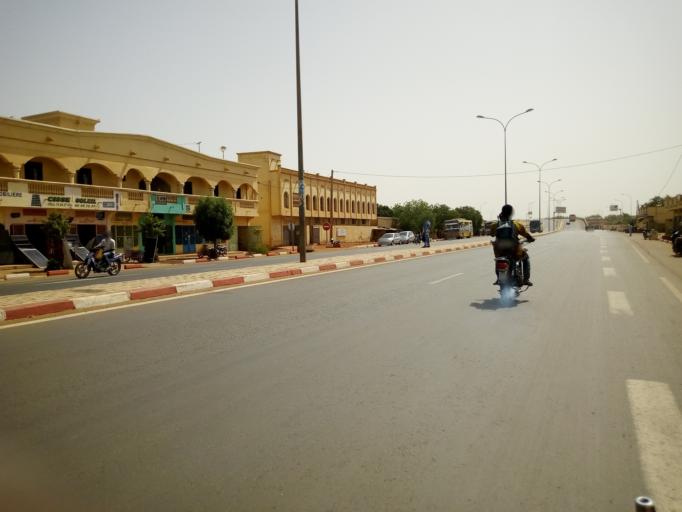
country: ML
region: Segou
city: Segou
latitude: 13.4363
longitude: -6.2420
